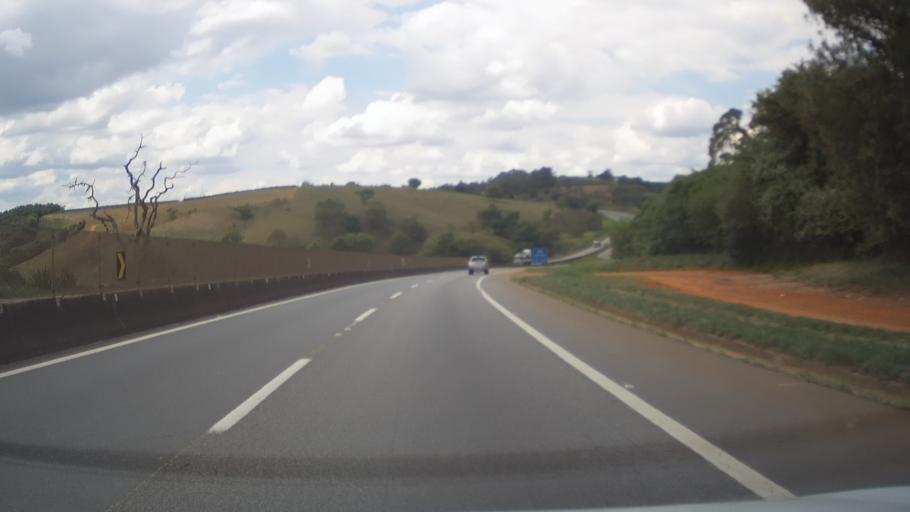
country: BR
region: Minas Gerais
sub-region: Nepomuceno
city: Nepomuceno
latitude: -21.2779
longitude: -45.1396
